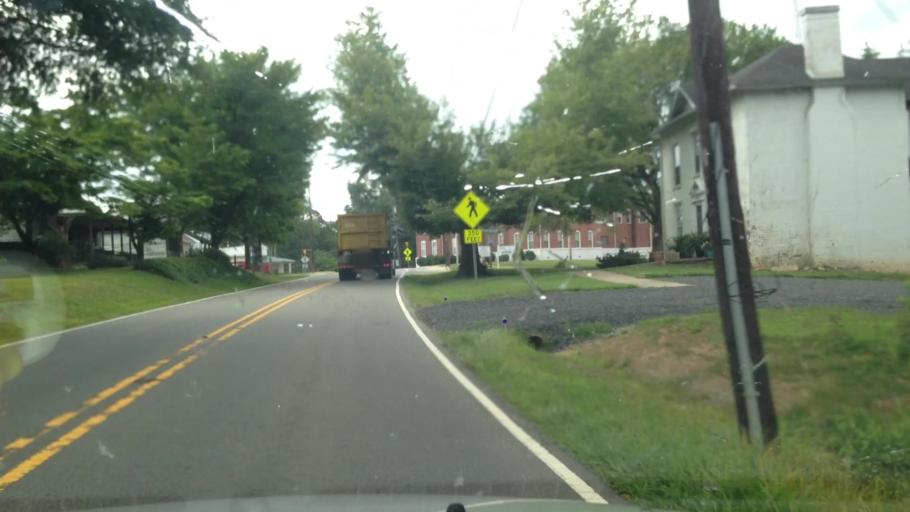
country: US
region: North Carolina
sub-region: Rockingham County
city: Wentworth
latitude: 36.3993
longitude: -79.7720
